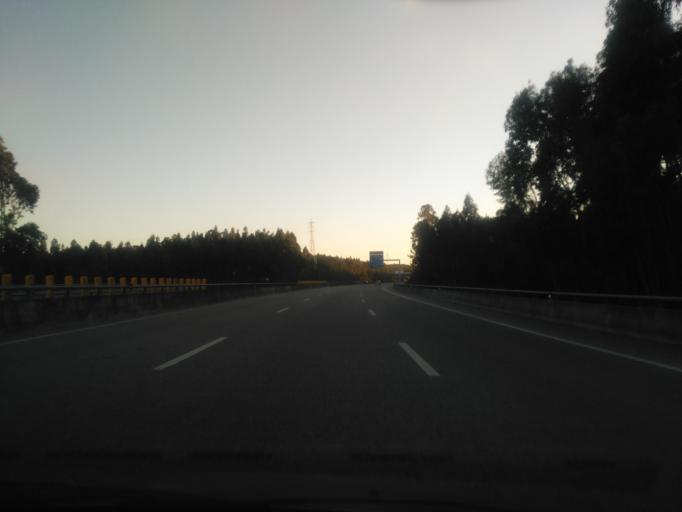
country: PT
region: Leiria
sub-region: Leiria
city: Maceira
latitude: 39.7265
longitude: -8.8952
